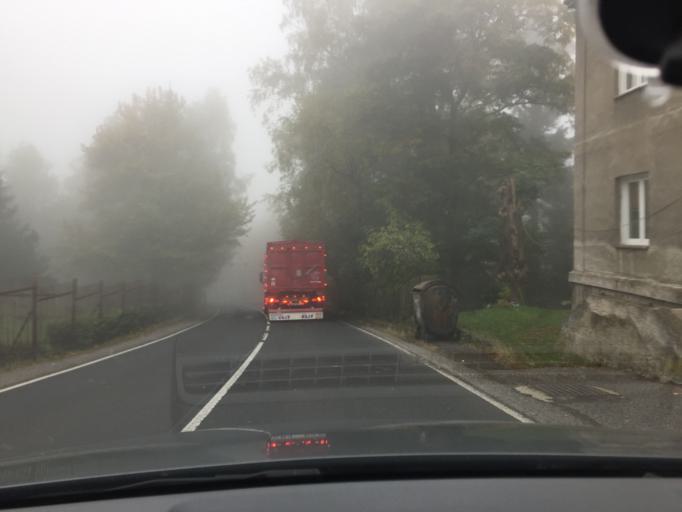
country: CZ
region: Ustecky
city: Libouchec
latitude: 50.7841
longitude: 14.0316
